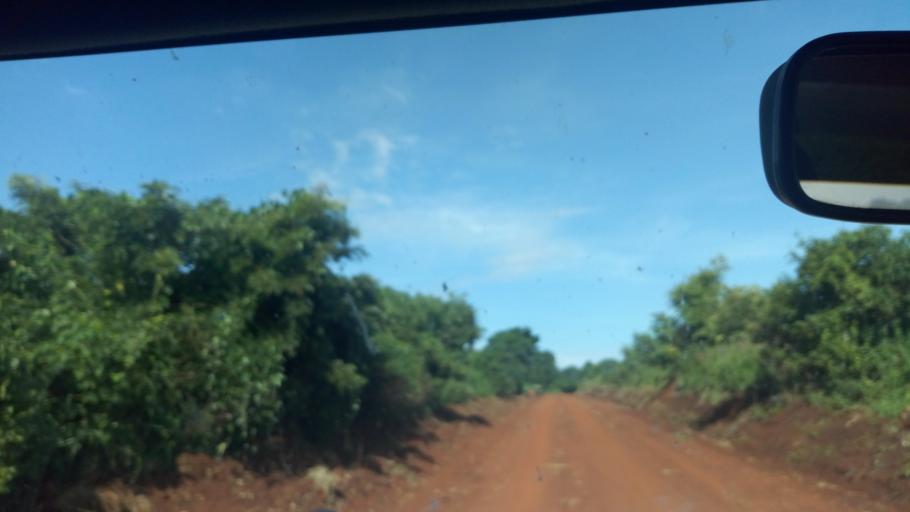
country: UG
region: Western Region
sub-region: Masindi District
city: Masindi
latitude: 1.6451
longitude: 31.7739
